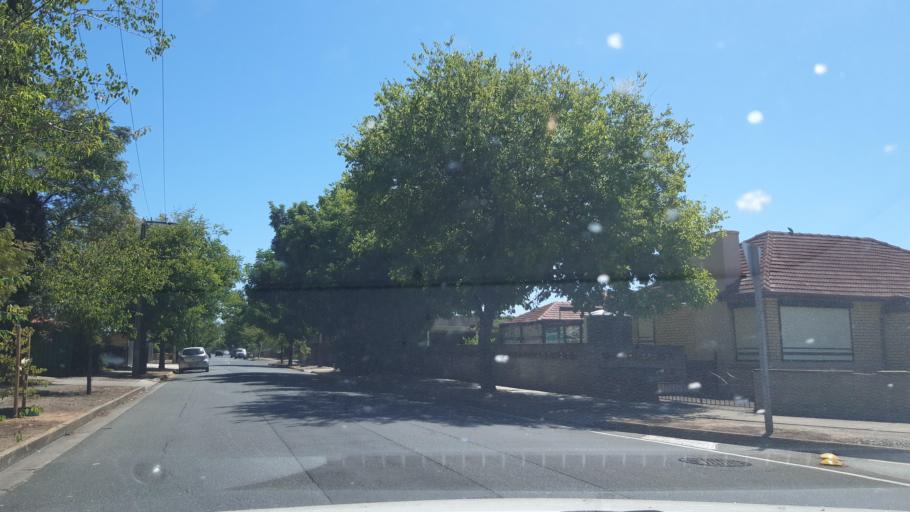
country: AU
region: South Australia
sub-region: Marion
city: Clovelly Park
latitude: -34.9889
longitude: 138.5683
